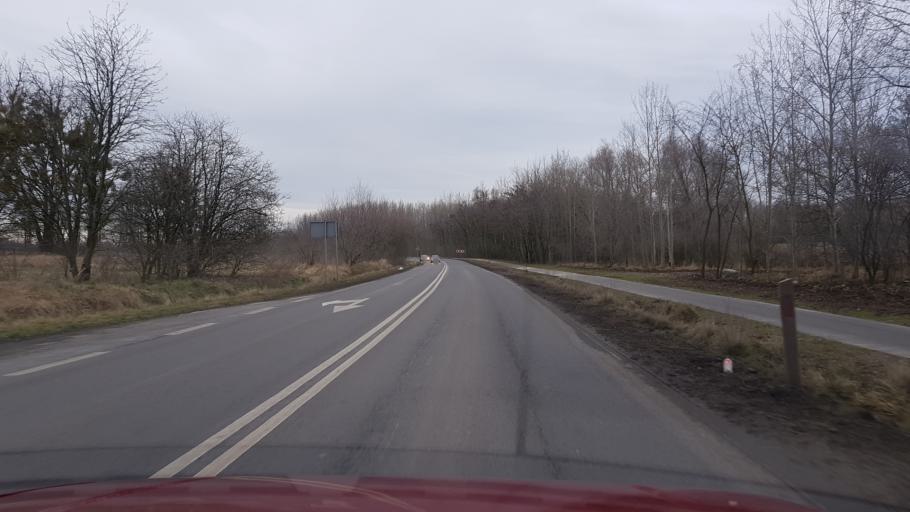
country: PL
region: West Pomeranian Voivodeship
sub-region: Powiat policki
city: Police
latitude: 53.5842
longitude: 14.5518
